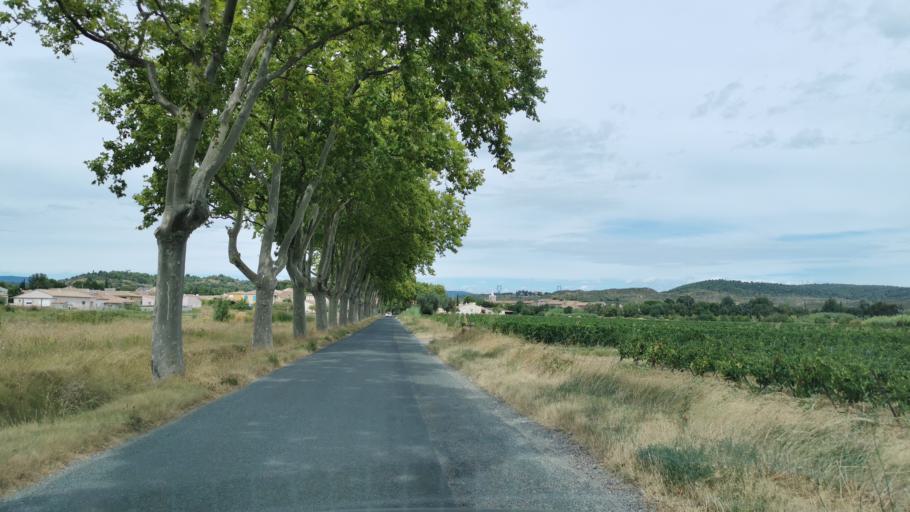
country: FR
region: Languedoc-Roussillon
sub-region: Departement de l'Aude
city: Bize-Minervois
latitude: 43.2966
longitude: 2.8278
